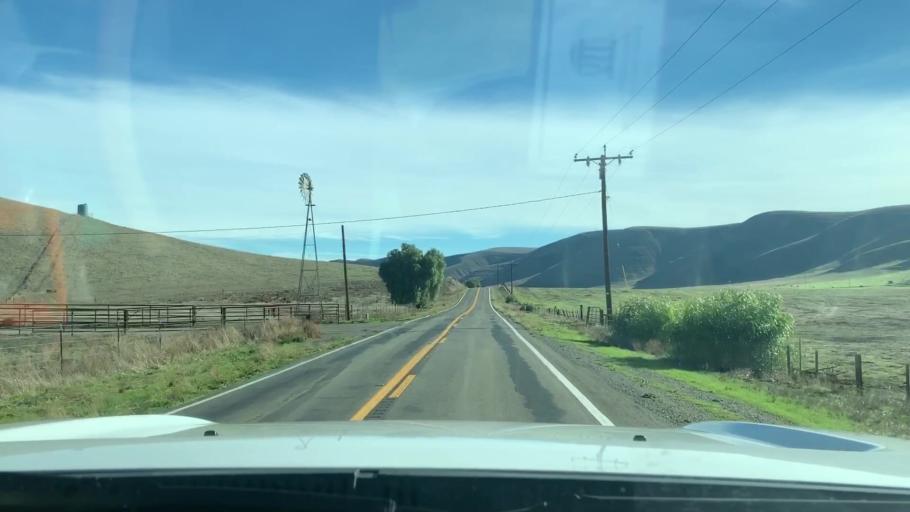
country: US
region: California
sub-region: Monterey County
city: King City
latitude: 36.1501
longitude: -120.9372
